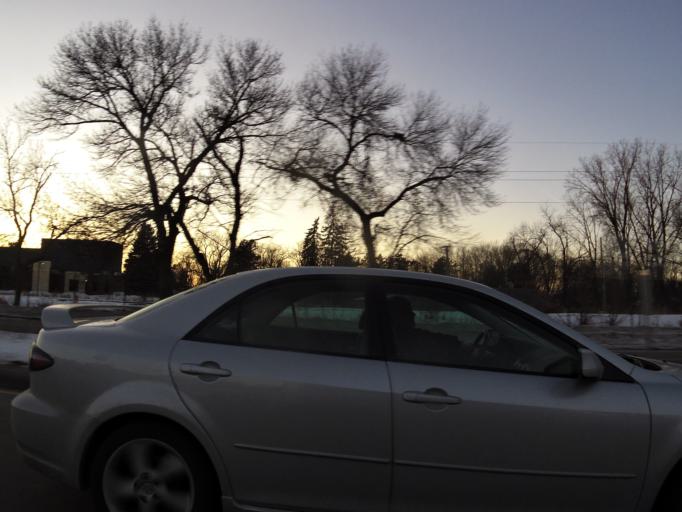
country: US
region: Minnesota
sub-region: Ramsey County
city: White Bear Lake
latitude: 45.0912
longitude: -93.0068
